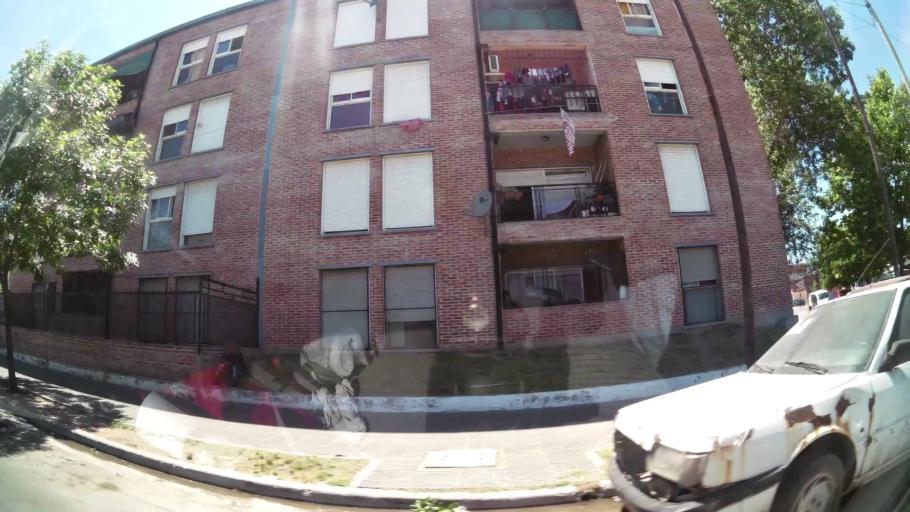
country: AR
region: Buenos Aires
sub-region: Partido de Avellaneda
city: Avellaneda
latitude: -34.6505
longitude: -58.4035
